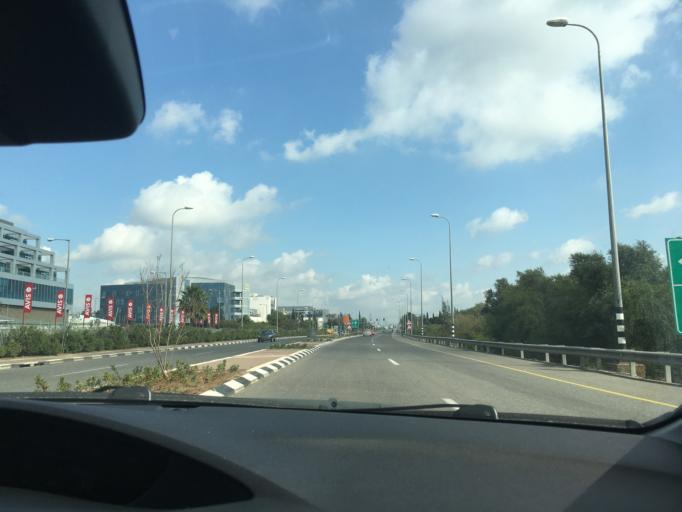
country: IL
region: Central District
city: Kfar Saba
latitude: 32.1741
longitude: 34.9335
